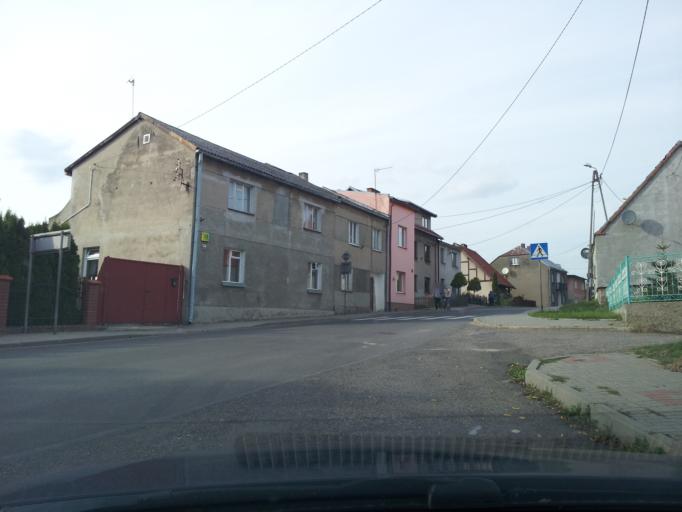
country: PL
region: Kujawsko-Pomorskie
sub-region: Powiat brodnicki
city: Gorzno
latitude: 53.1956
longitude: 19.6458
